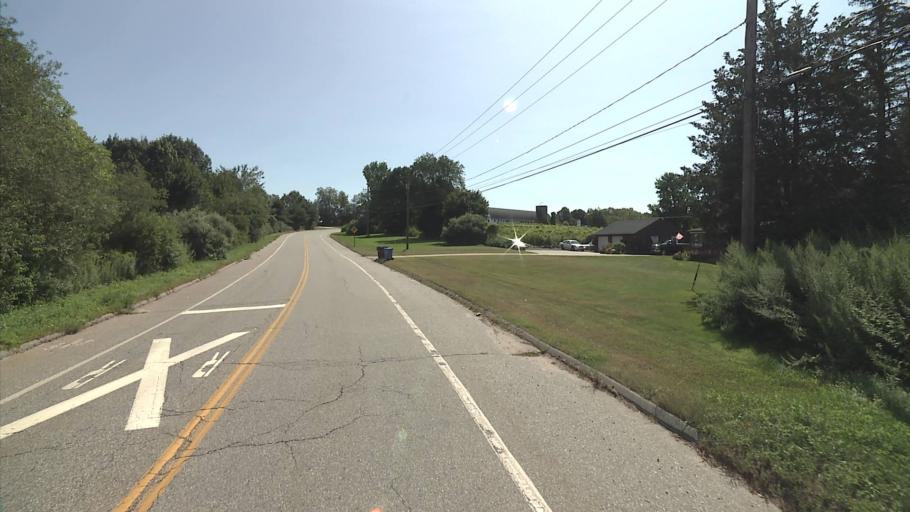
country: US
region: Connecticut
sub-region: Windham County
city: South Windham
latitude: 41.6358
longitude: -72.1675
